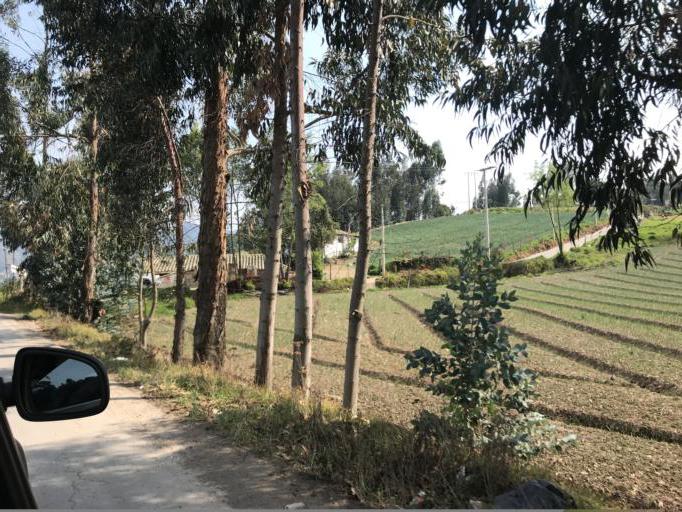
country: CO
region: Boyaca
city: Samaca
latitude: 5.5043
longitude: -73.4983
